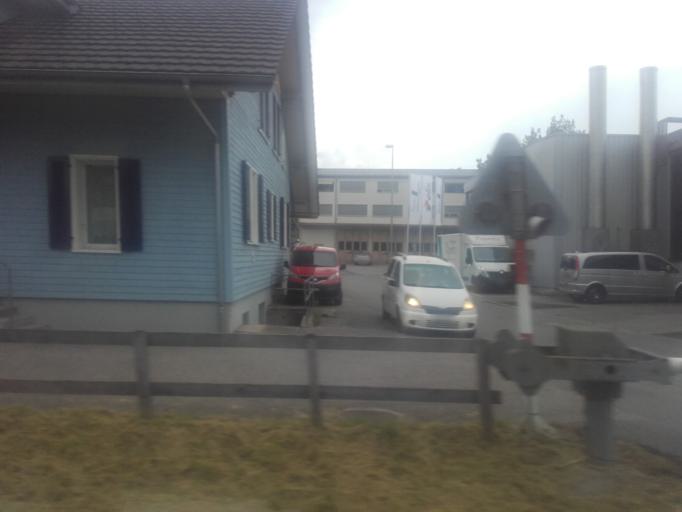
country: CH
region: Bern
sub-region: Emmental District
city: Kirchberg
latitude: 47.0944
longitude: 7.5622
